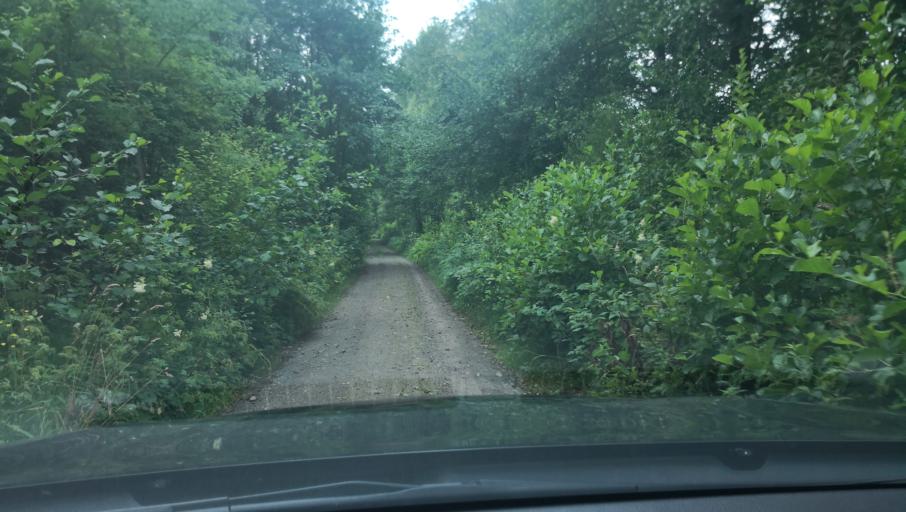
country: SE
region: Skane
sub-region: Simrishamns Kommun
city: Kivik
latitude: 55.6291
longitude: 14.1274
